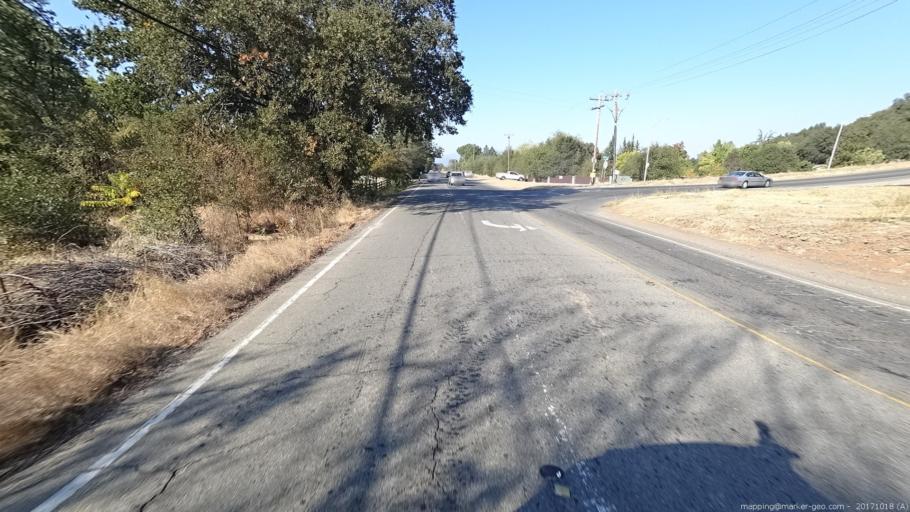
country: US
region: California
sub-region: Shasta County
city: Redding
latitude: 40.5347
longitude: -122.3360
